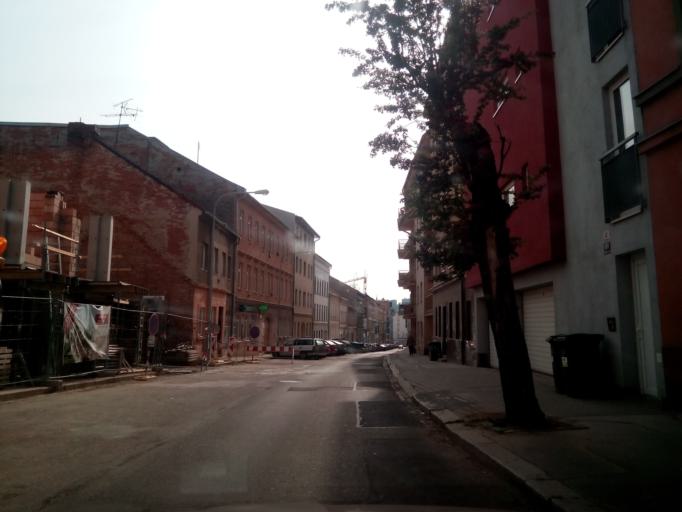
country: CZ
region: South Moravian
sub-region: Mesto Brno
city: Brno
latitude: 49.2022
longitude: 16.6206
